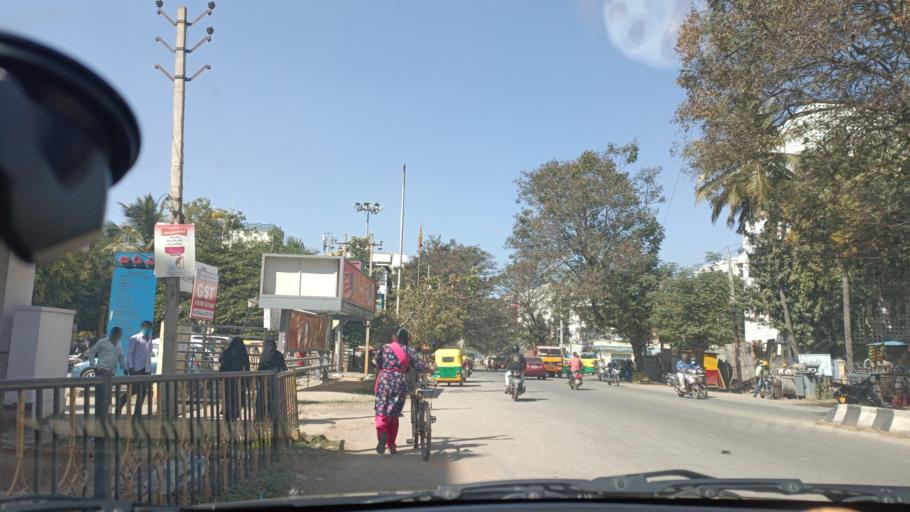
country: IN
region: Karnataka
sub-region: Bangalore Urban
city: Bangalore
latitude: 13.0258
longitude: 77.6284
